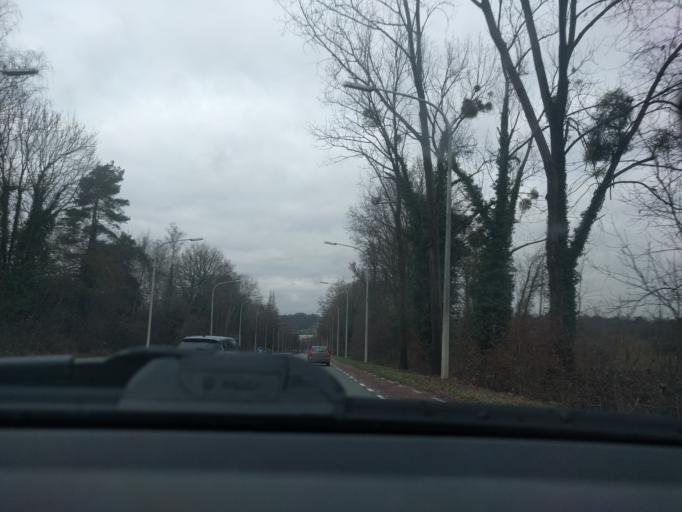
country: BE
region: Wallonia
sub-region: Province de Namur
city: Namur
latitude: 50.4567
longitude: 4.8925
